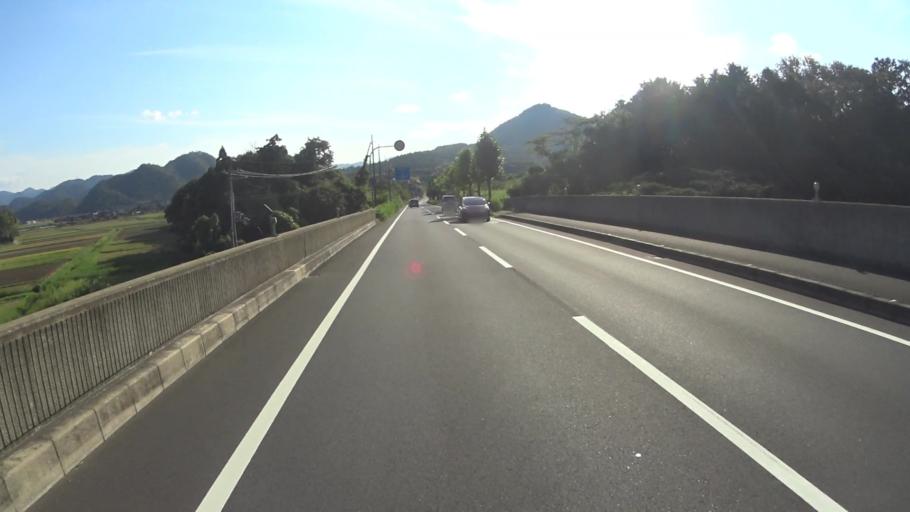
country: JP
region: Hyogo
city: Toyooka
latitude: 35.6192
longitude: 134.9251
